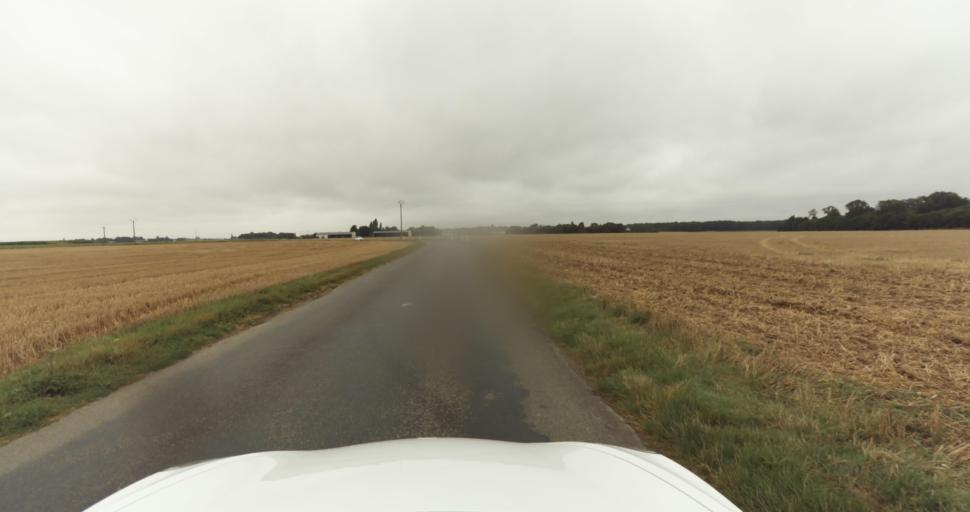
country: FR
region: Haute-Normandie
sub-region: Departement de l'Eure
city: Aviron
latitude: 49.0640
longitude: 1.1224
